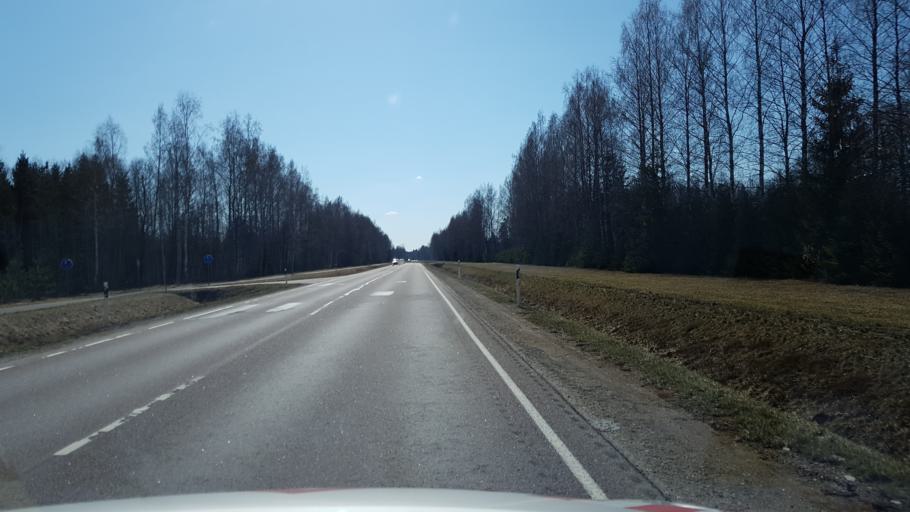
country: EE
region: Jogevamaa
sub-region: Mustvee linn
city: Mustvee
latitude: 58.7741
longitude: 26.9119
